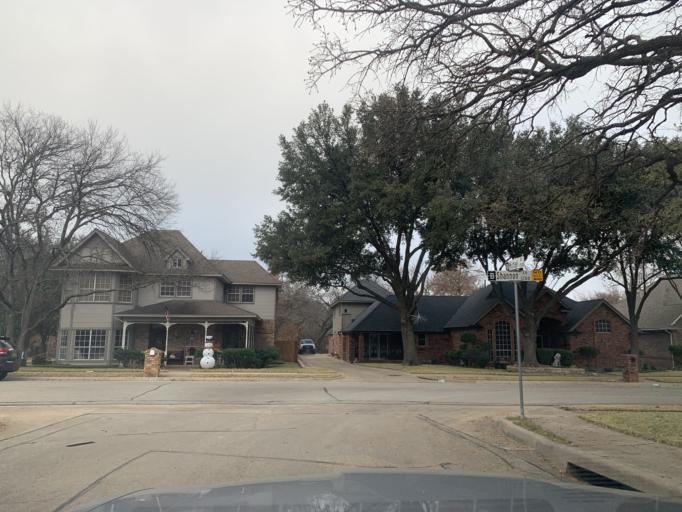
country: US
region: Texas
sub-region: Tarrant County
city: Bedford
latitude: 32.8300
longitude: -97.1457
